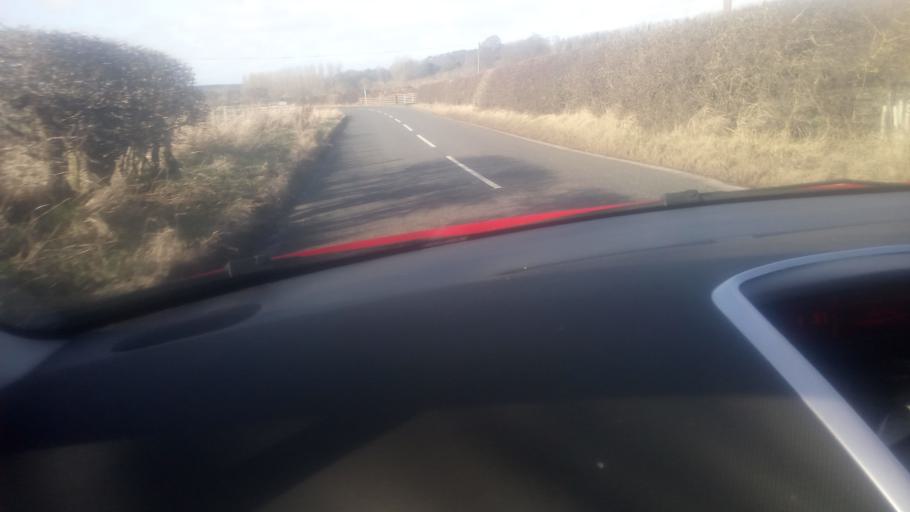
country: GB
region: Scotland
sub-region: The Scottish Borders
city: Kelso
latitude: 55.5349
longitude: -2.4504
